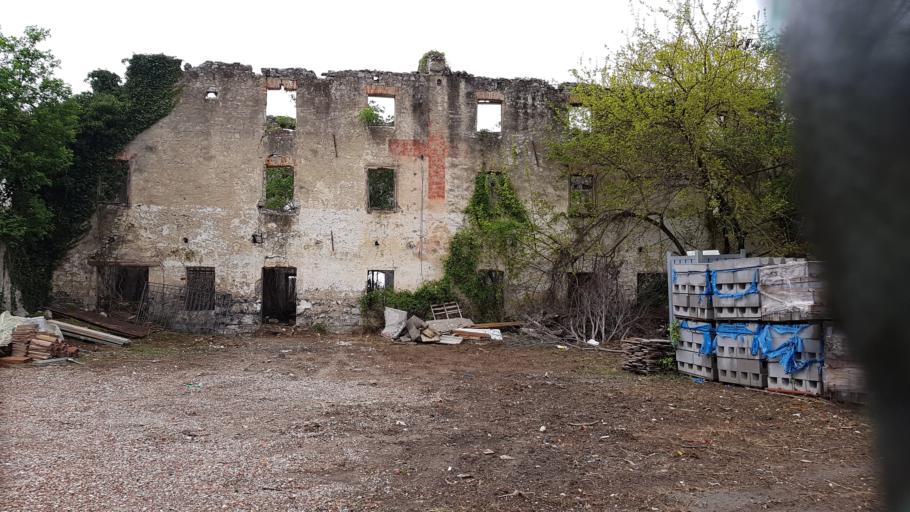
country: IT
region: Friuli Venezia Giulia
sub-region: Provincia di Gorizia
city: Begliano
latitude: 45.8194
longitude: 13.4574
